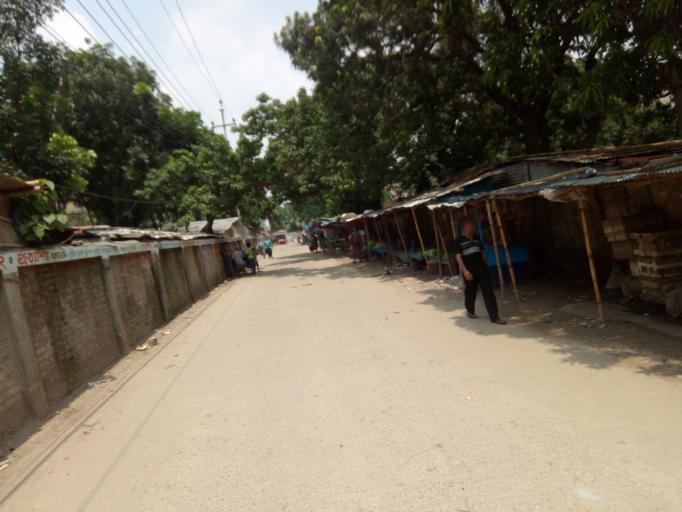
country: BD
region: Dhaka
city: Paltan
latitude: 23.7387
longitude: 90.4238
